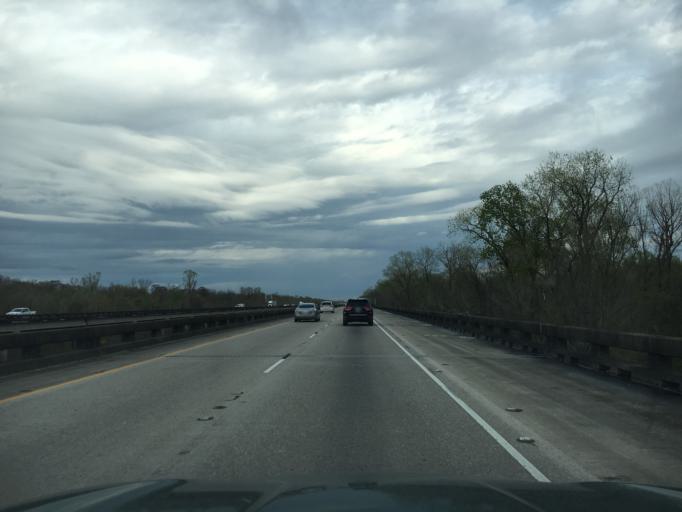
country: US
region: Louisiana
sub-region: Iberville Parish
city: Maringouin
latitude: 30.3713
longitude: -91.6151
